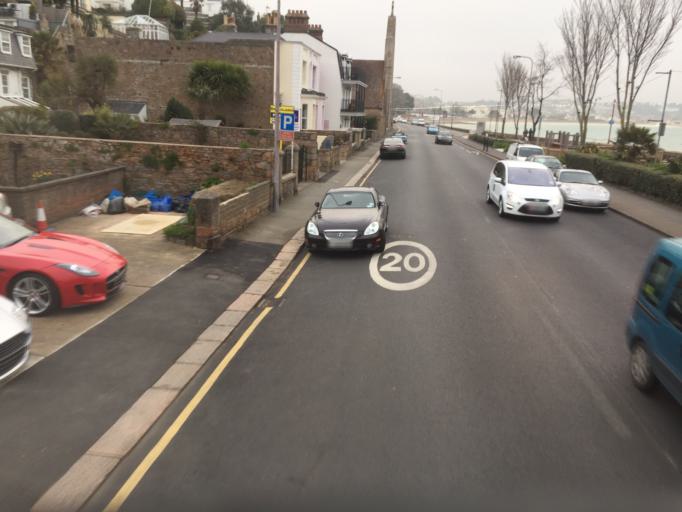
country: JE
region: St Helier
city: Saint Helier
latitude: 49.1884
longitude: -2.1697
